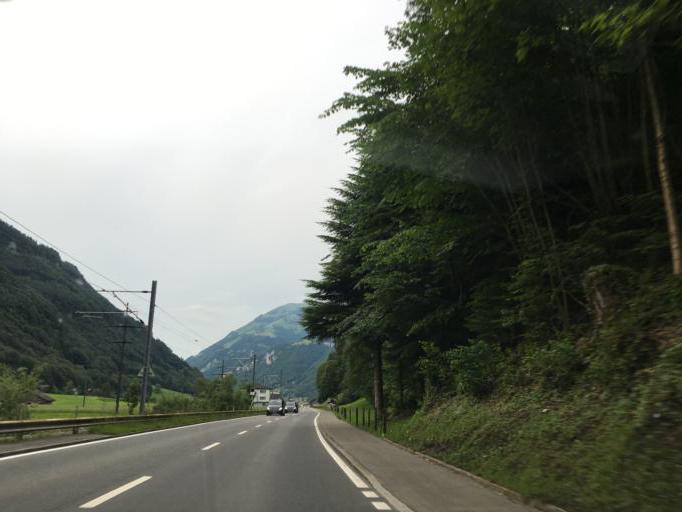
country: CH
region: Nidwalden
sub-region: Nidwalden
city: Wolfenschiessen
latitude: 46.8823
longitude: 8.3785
